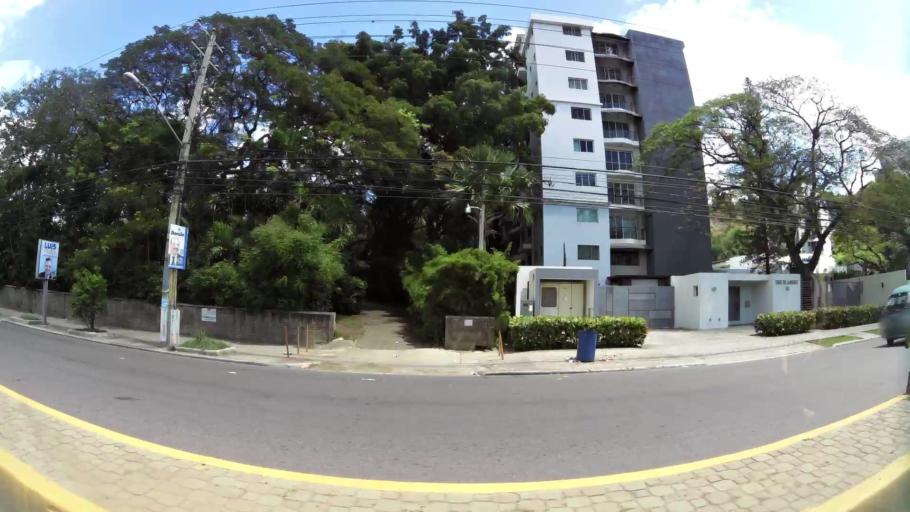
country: DO
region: Santiago
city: Santiago de los Caballeros
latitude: 19.4654
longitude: -70.6866
